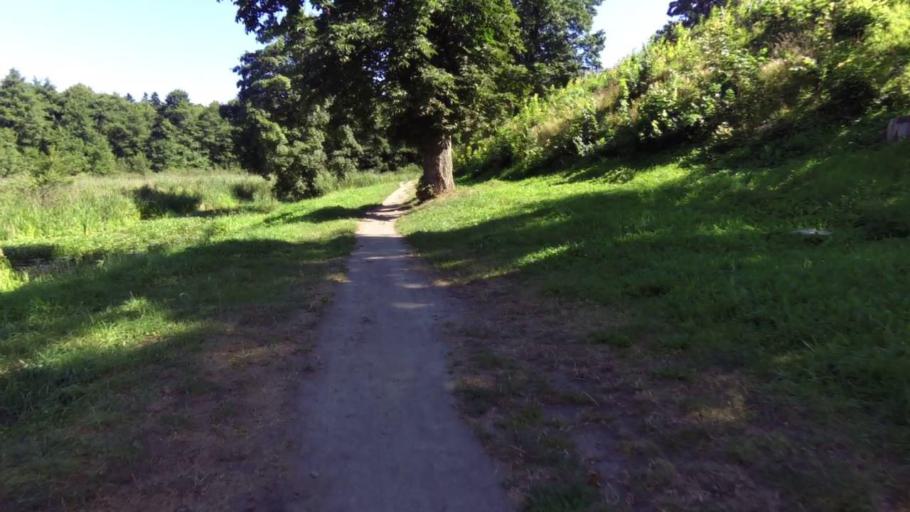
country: PL
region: West Pomeranian Voivodeship
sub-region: Powiat drawski
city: Zlocieniec
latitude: 53.5356
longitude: 16.0060
